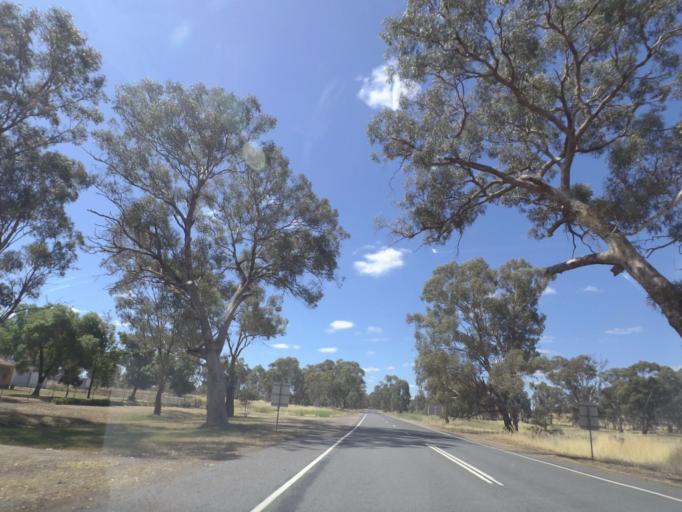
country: AU
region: Victoria
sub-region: Wangaratta
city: Wangaratta
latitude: -36.4096
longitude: 146.2699
